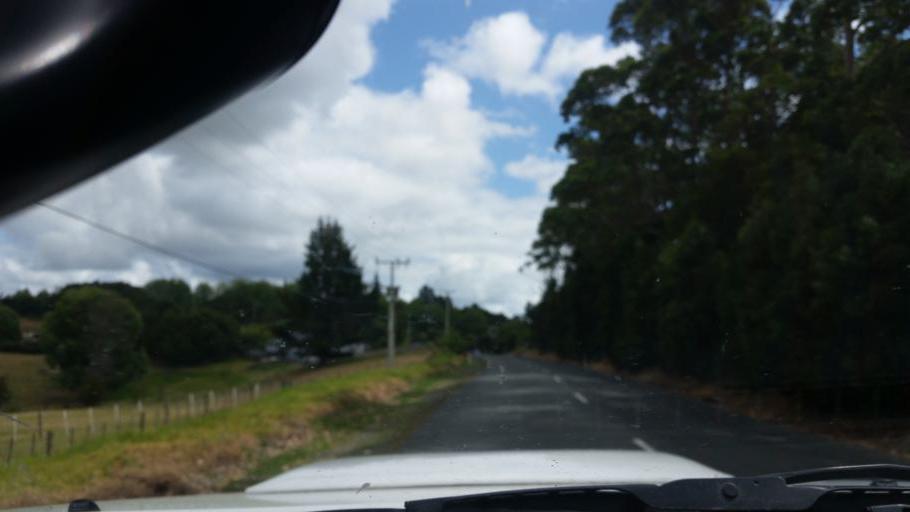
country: NZ
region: Auckland
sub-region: Auckland
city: Wellsford
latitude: -36.1331
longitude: 174.5565
